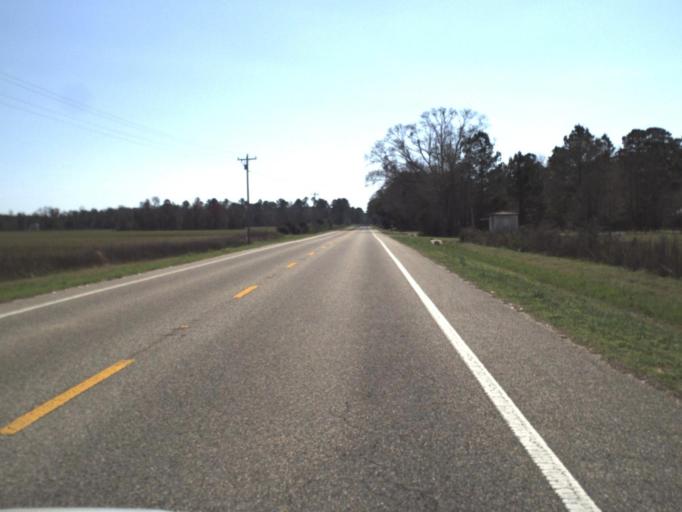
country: US
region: Florida
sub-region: Calhoun County
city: Blountstown
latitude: 30.5701
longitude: -85.0218
